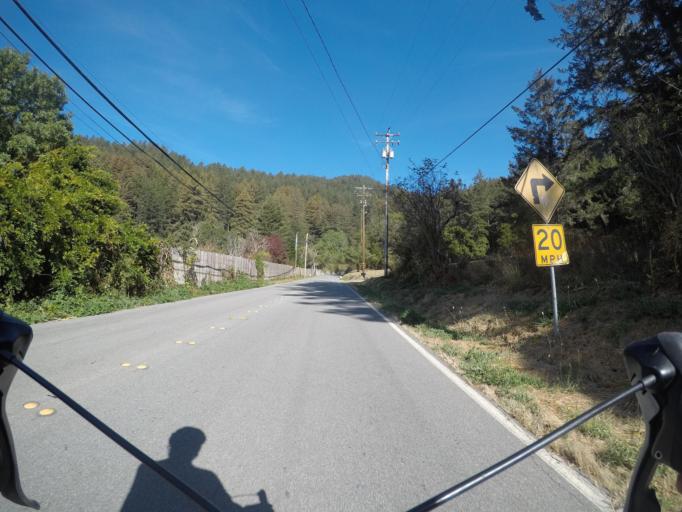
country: US
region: California
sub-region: San Mateo County
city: Portola Valley
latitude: 37.2665
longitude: -122.3223
